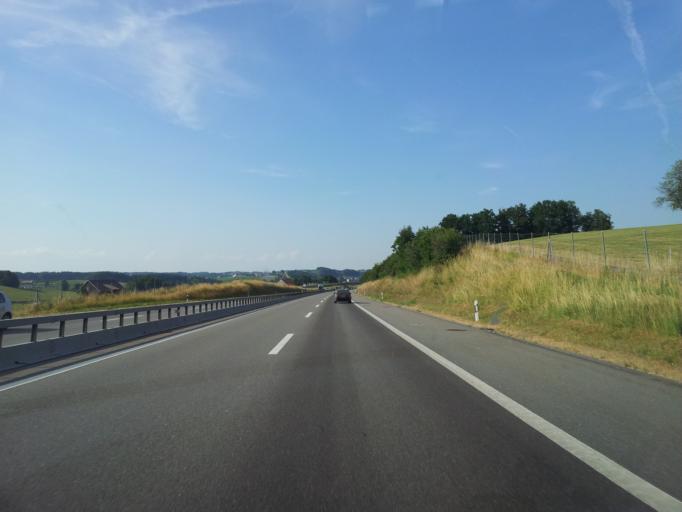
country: CH
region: Fribourg
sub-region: Veveyse District
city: Chatel-Saint-Denis
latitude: 46.5513
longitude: 6.9152
